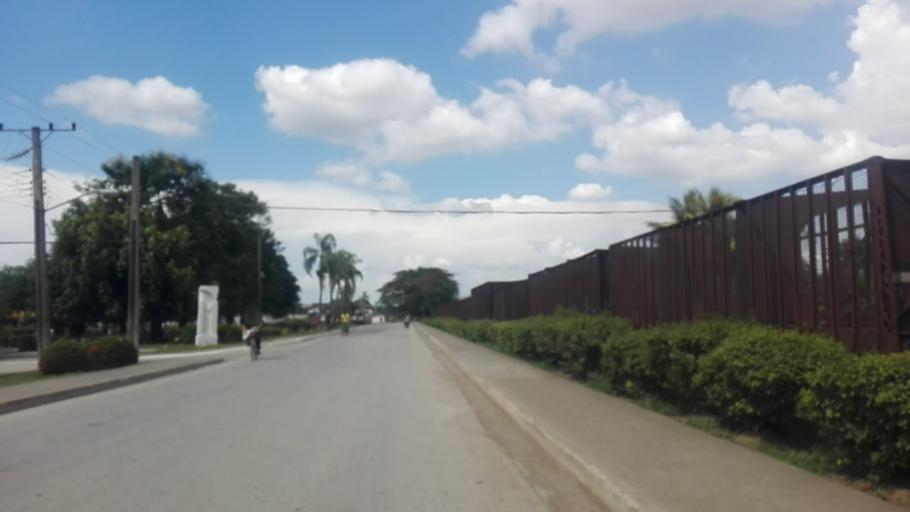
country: CU
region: Granma
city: Bartolome Maso
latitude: 20.1669
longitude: -76.9451
